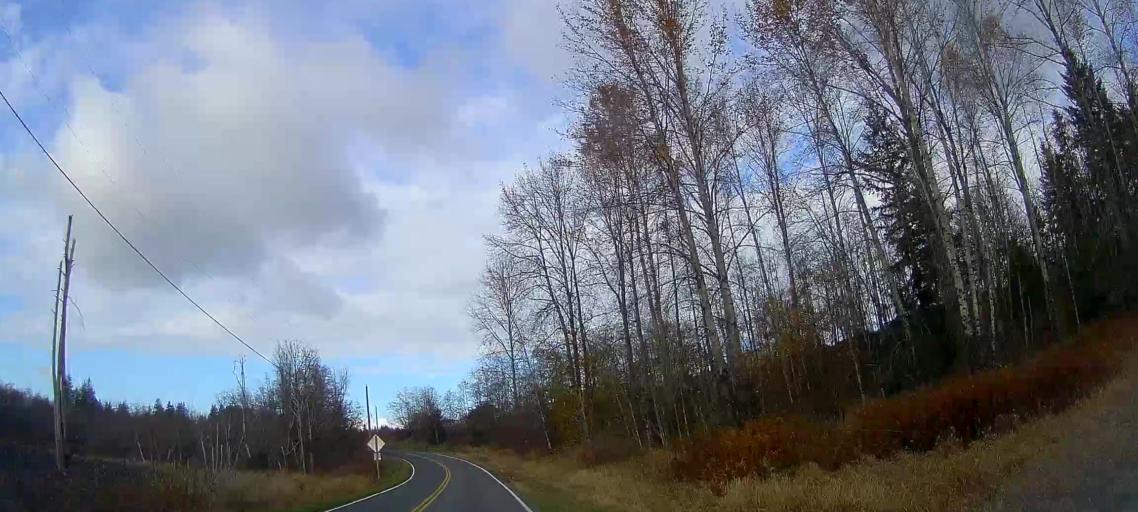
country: US
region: Washington
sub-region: Skagit County
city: Big Lake
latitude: 48.4093
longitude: -122.2184
